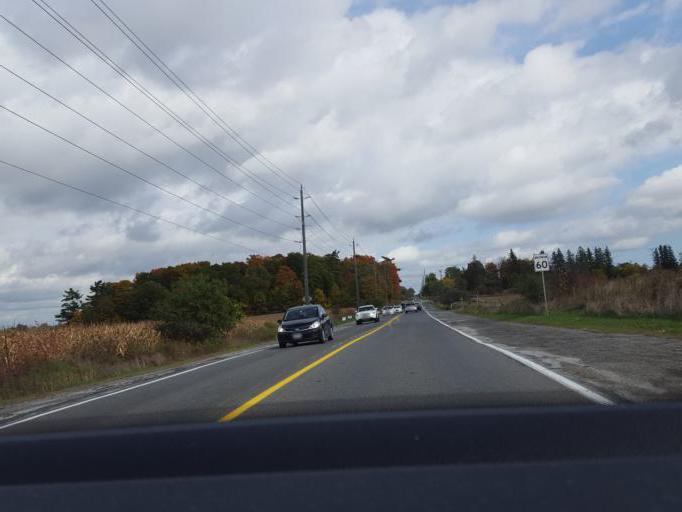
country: CA
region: Ontario
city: Markham
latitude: 43.8430
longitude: -79.2233
